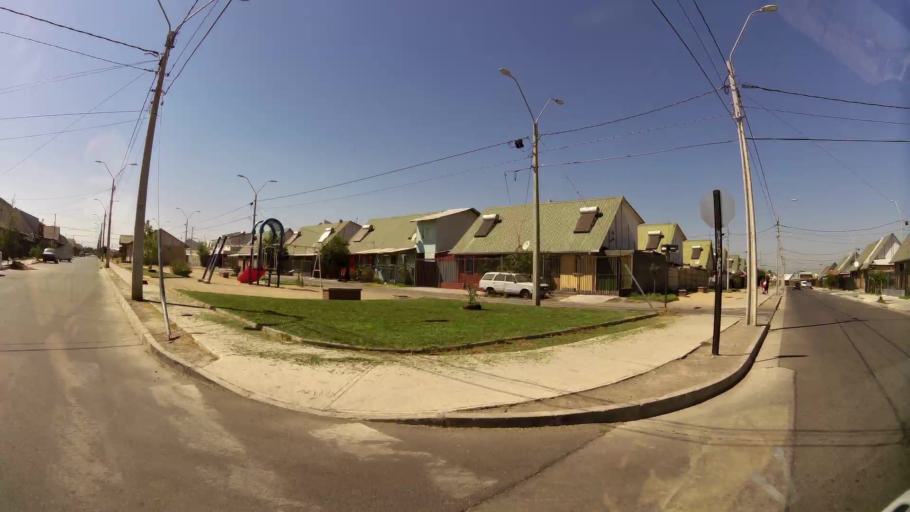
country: CL
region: Maule
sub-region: Provincia de Curico
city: Curico
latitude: -34.9616
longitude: -71.2359
